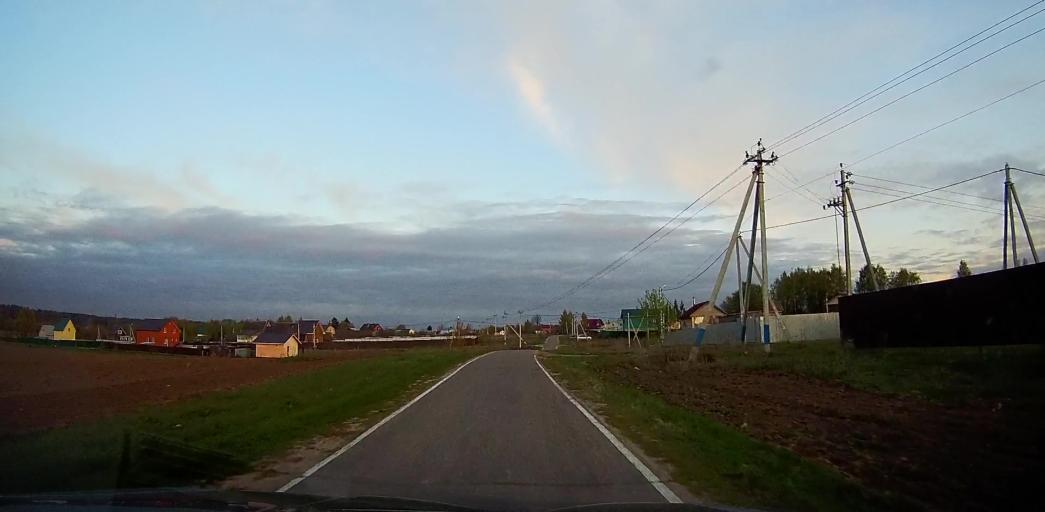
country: RU
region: Moskovskaya
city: Peski
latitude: 55.2146
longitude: 38.7389
